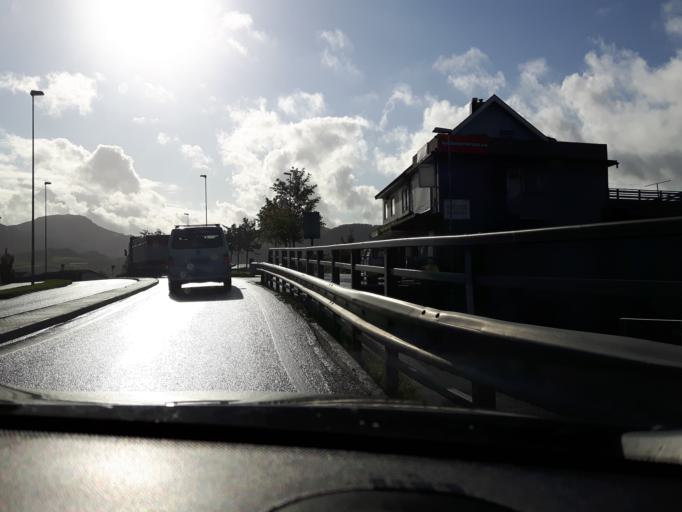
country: NO
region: Rogaland
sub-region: Gjesdal
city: Algard
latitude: 58.7668
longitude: 5.8626
